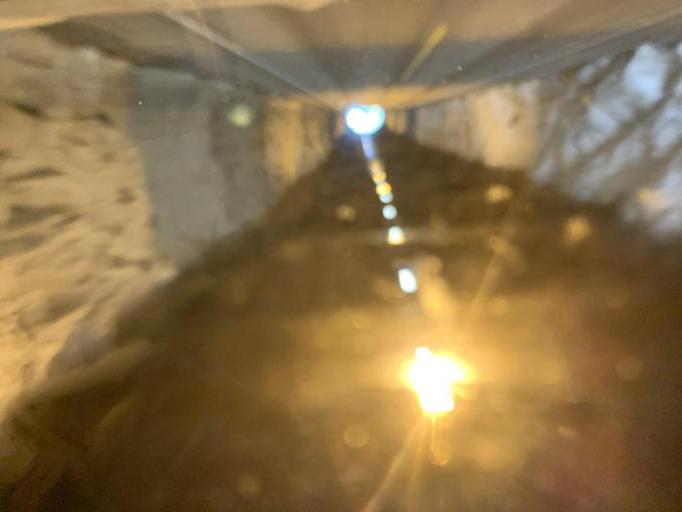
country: NO
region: Rogaland
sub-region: Eigersund
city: Egersund
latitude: 58.4627
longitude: 5.9874
